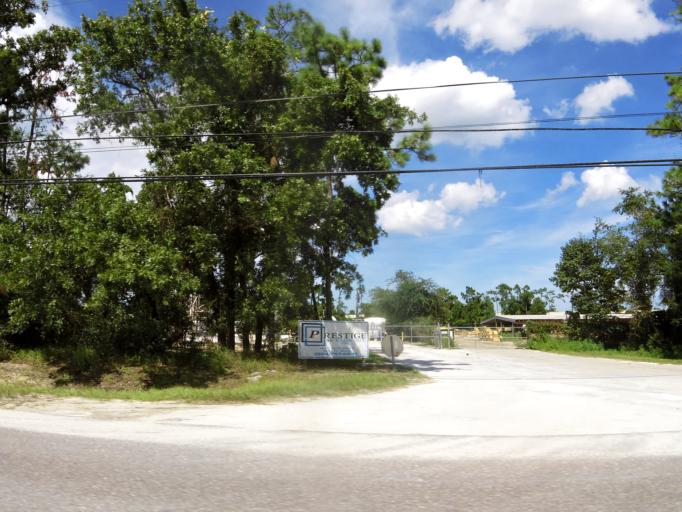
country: US
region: Florida
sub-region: Duval County
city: Jacksonville
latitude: 30.4202
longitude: -81.5696
